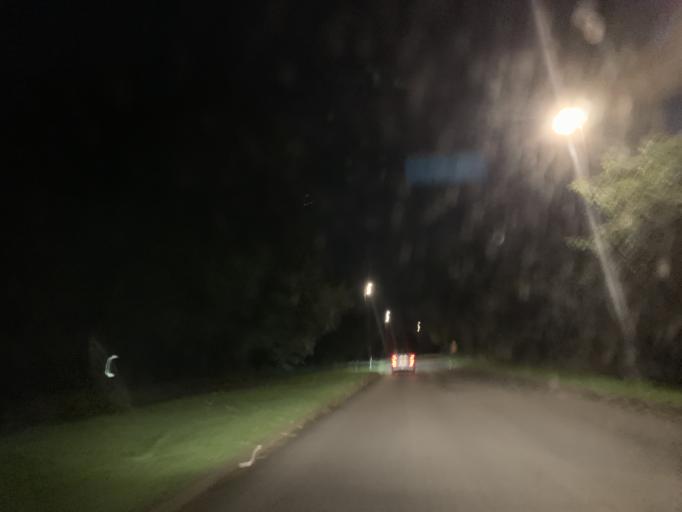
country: GB
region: England
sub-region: Hampshire
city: Eastleigh
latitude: 50.9334
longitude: -1.3732
